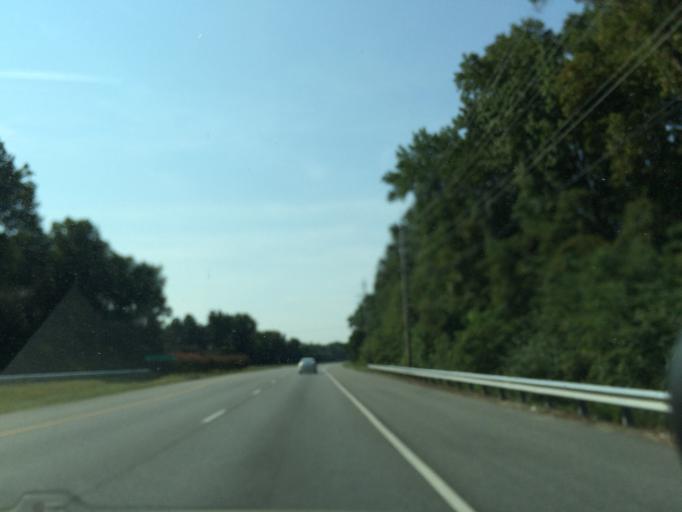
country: US
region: Maryland
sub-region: Charles County
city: La Plata
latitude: 38.5229
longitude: -76.9821
